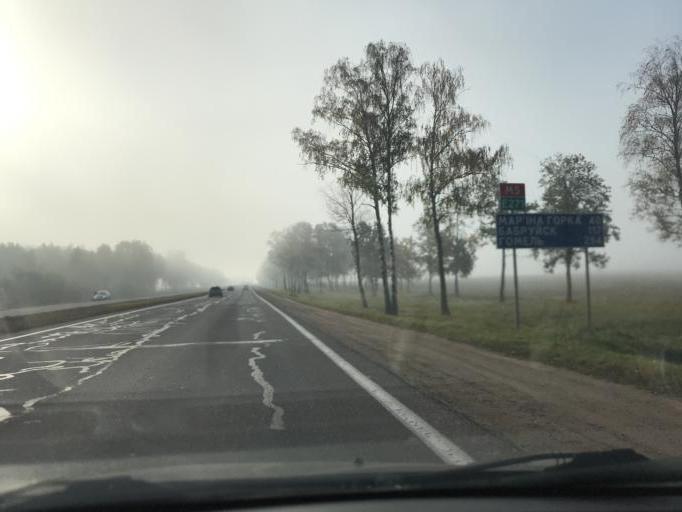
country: BY
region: Minsk
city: Luhavaya Slabada
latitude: 53.7856
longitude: 27.8218
